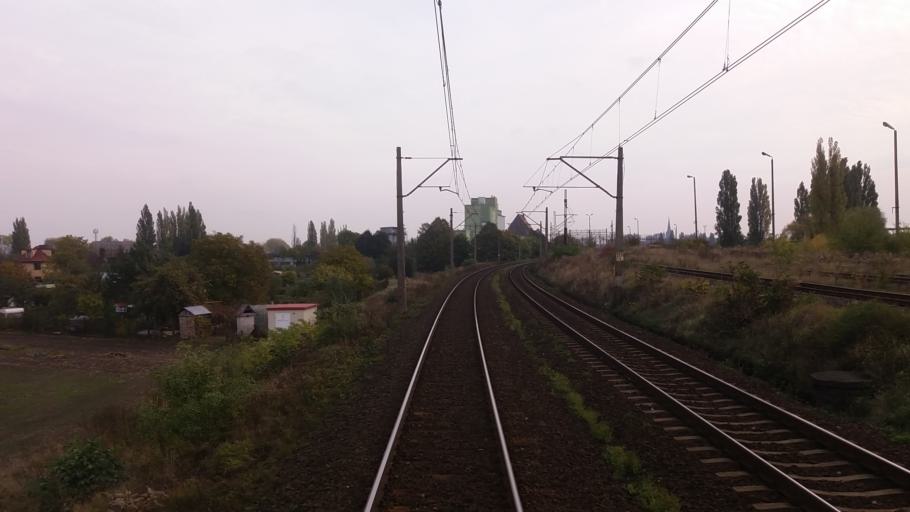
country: PL
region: West Pomeranian Voivodeship
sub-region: Powiat stargardzki
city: Stargard Szczecinski
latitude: 53.3520
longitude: 15.0143
